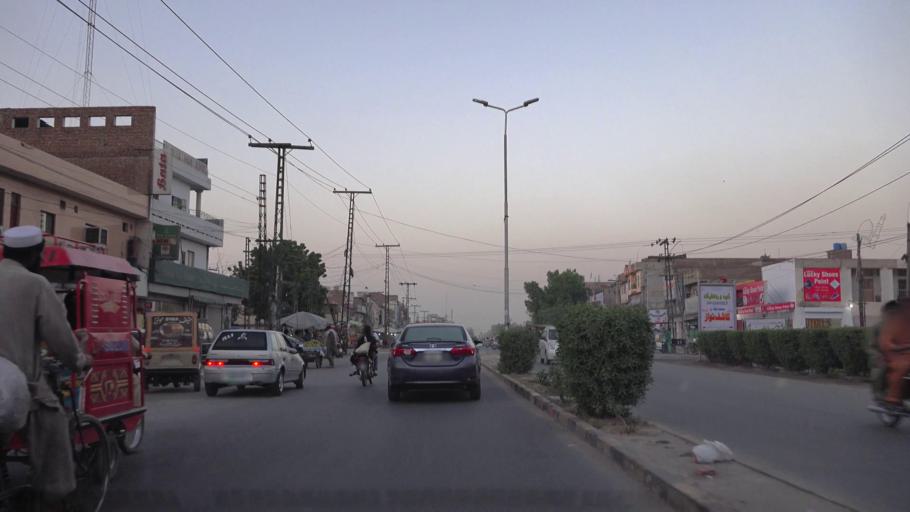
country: PK
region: Punjab
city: Faisalabad
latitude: 31.4490
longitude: 73.0974
